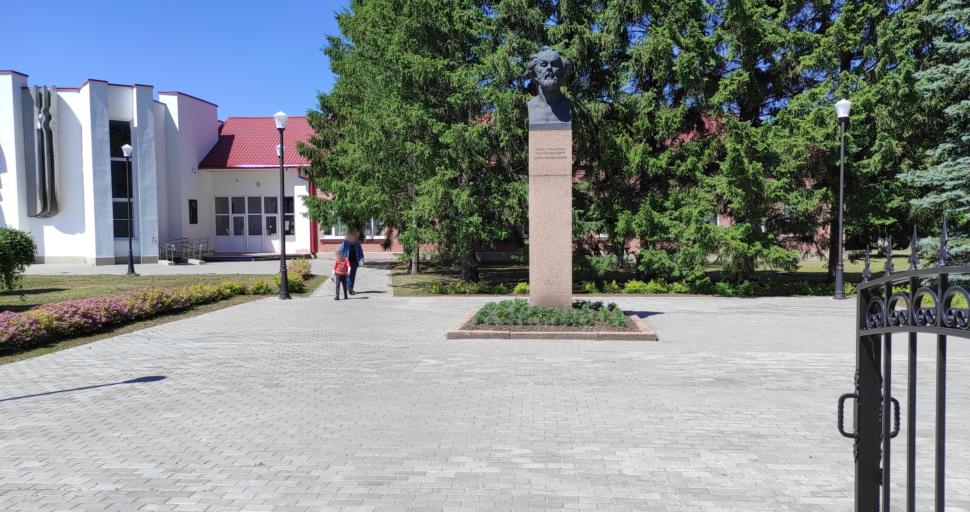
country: RU
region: Rjazan
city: Izhevskoye
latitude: 54.5492
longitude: 40.8542
